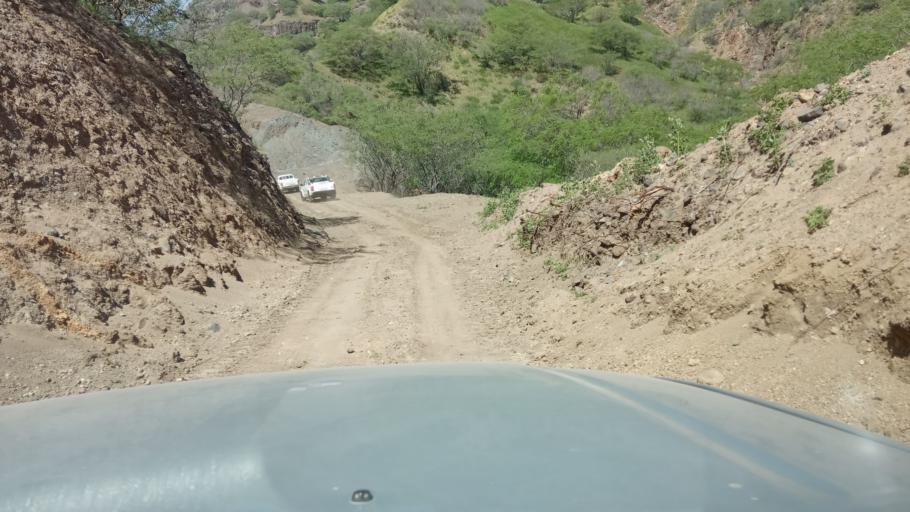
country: CV
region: Santa Catarina
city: Assomada
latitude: 15.1150
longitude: -23.7285
